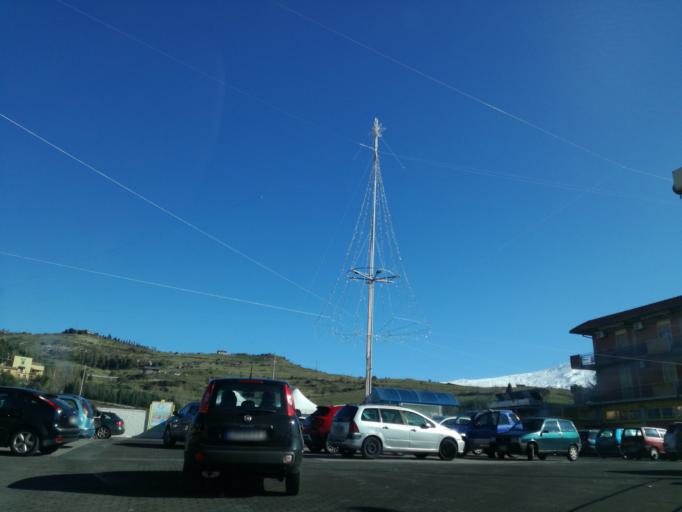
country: IT
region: Sicily
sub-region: Catania
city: Bronte
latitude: 37.7938
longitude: 14.8470
